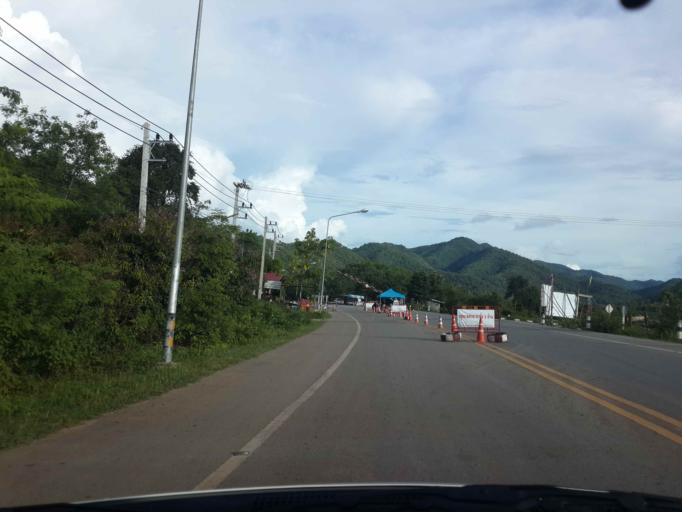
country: TH
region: Kanchanaburi
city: Sai Yok
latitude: 13.8831
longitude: 99.1713
